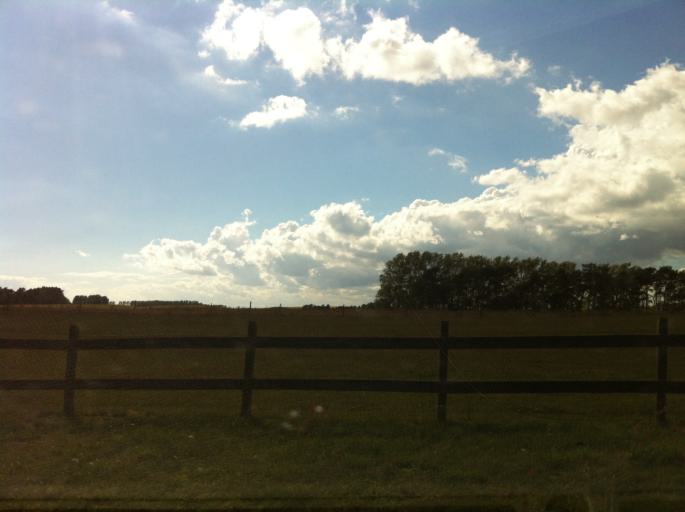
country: SE
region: Skane
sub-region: Ystads Kommun
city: Kopingebro
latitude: 55.3901
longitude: 14.0568
